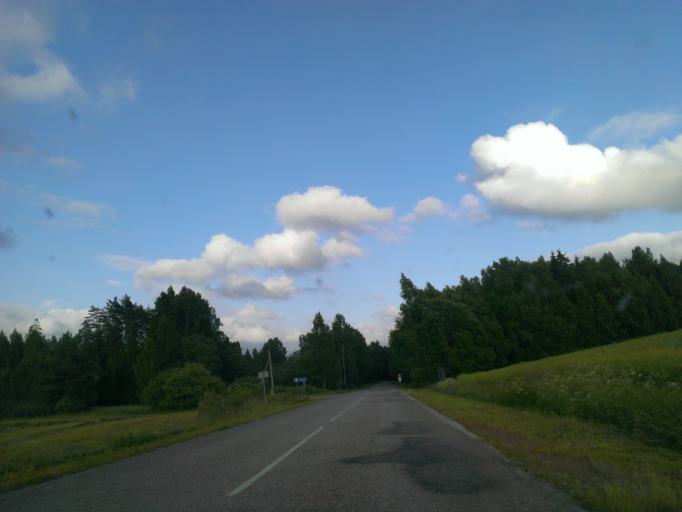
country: LV
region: Skrunda
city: Skrunda
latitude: 56.6899
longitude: 21.8758
